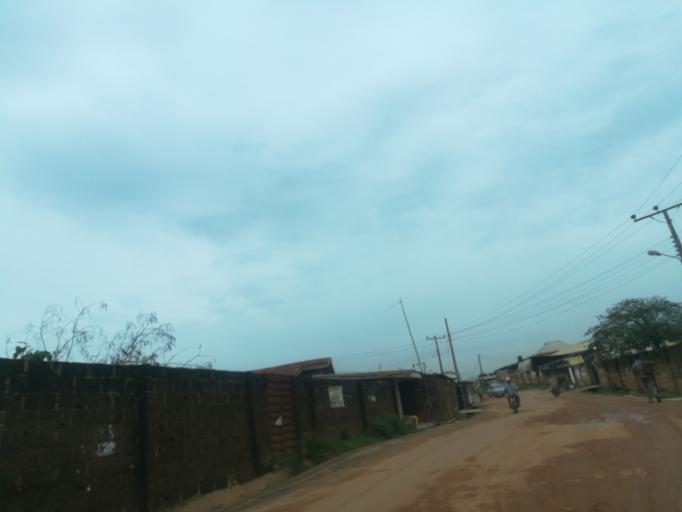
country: NG
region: Oyo
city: Egbeda
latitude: 7.3753
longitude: 3.9964
